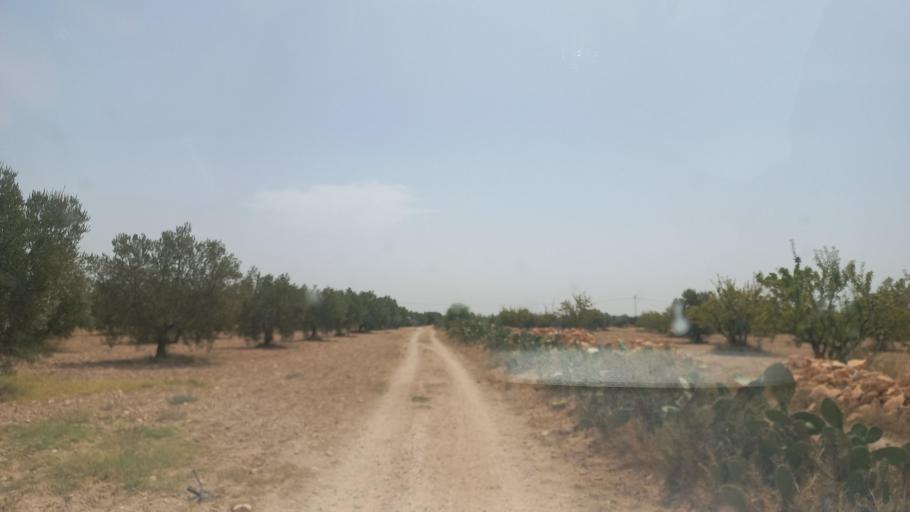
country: TN
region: Al Qasrayn
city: Kasserine
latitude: 35.2593
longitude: 9.0060
